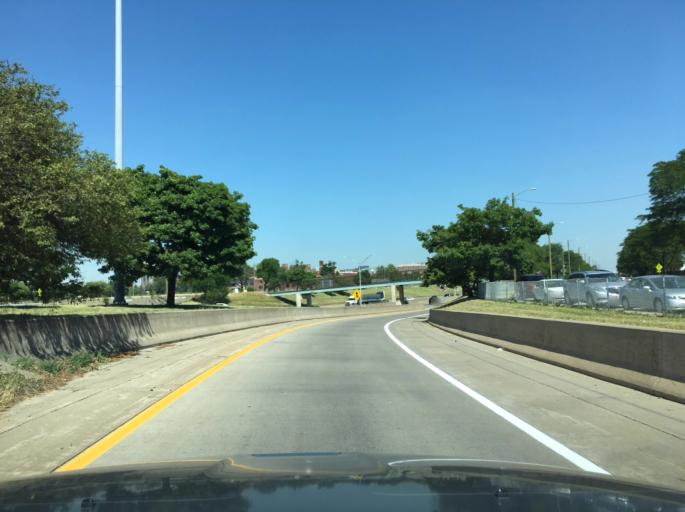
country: US
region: Michigan
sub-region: Wayne County
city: Detroit
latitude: 42.3451
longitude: -83.0433
